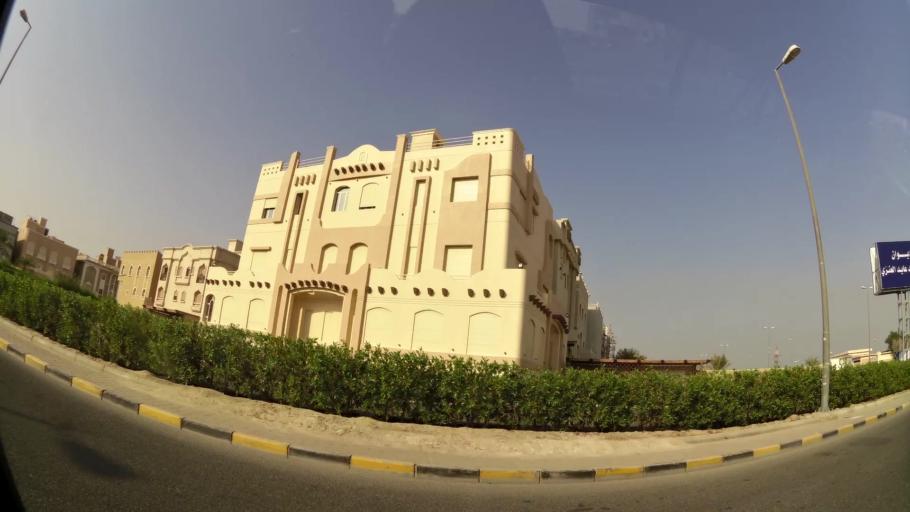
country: KW
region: Al Asimah
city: Ar Rabiyah
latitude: 29.3055
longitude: 47.8004
